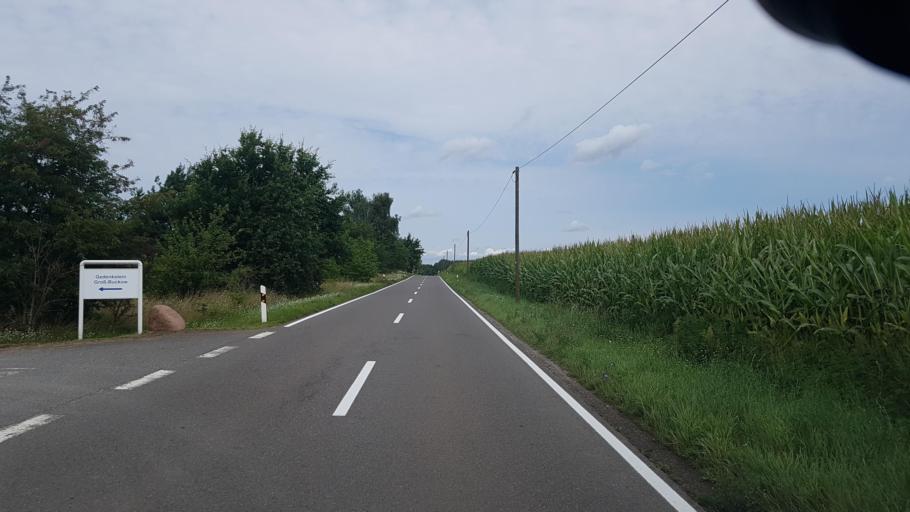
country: DE
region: Brandenburg
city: Spremberg
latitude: 51.6109
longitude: 14.3422
